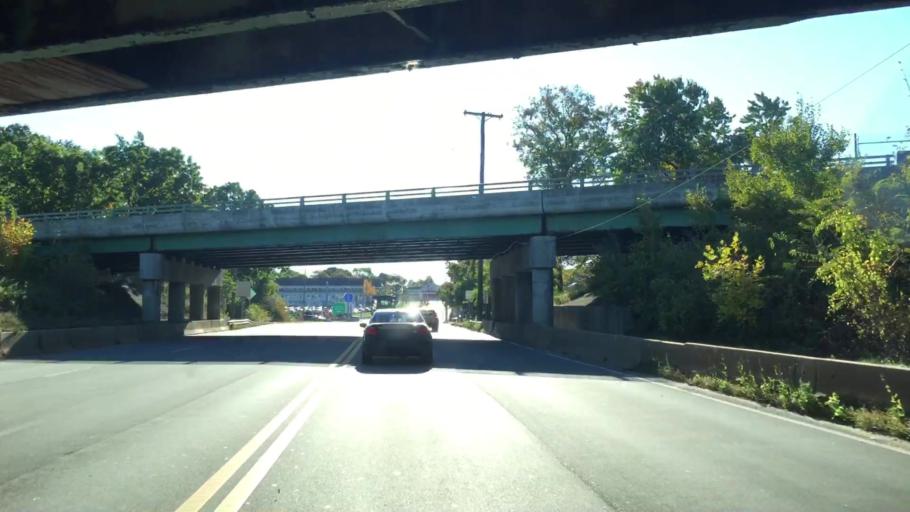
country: US
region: Massachusetts
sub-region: Middlesex County
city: Tewksbury
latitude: 42.6281
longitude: -71.2730
